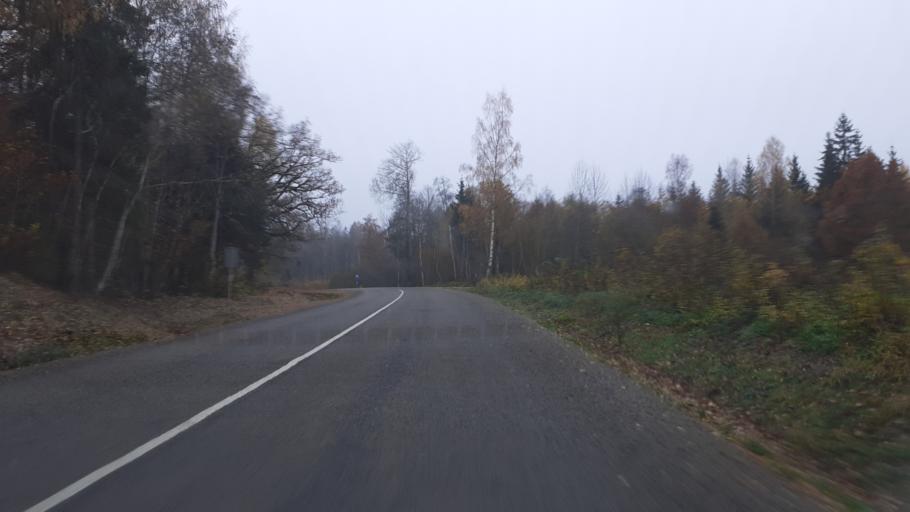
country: LV
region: Kuldigas Rajons
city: Kuldiga
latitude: 56.9519
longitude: 21.8657
